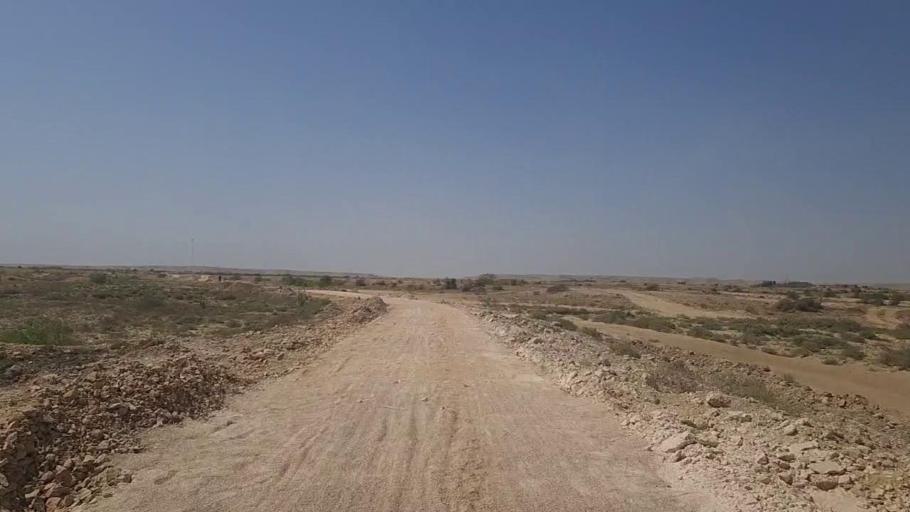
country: PK
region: Sindh
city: Kotri
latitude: 25.1529
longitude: 68.1512
